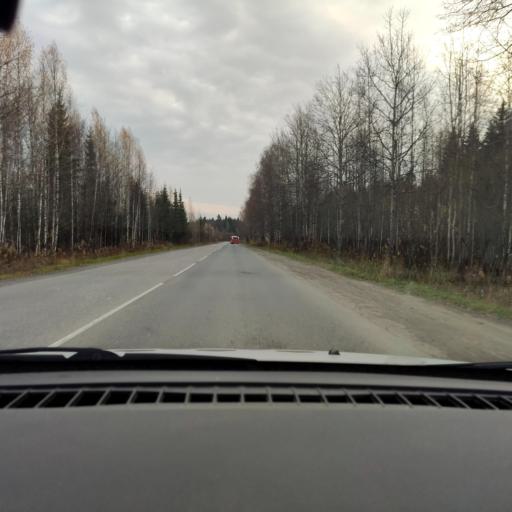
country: RU
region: Perm
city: Polazna
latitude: 58.1128
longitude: 56.4245
